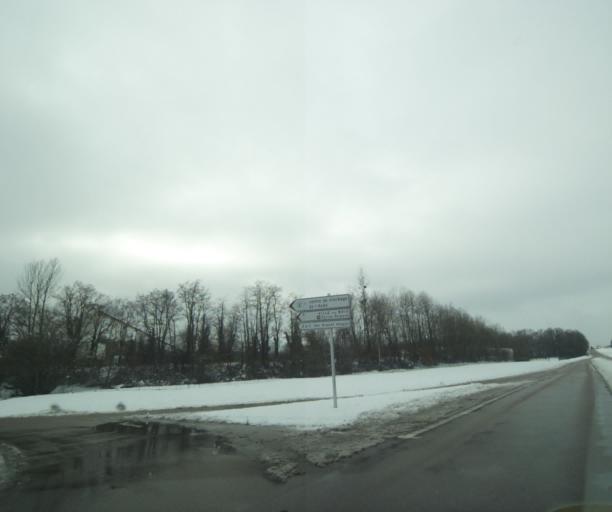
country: FR
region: Champagne-Ardenne
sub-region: Departement de la Haute-Marne
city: Montier-en-Der
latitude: 48.4286
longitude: 4.6742
